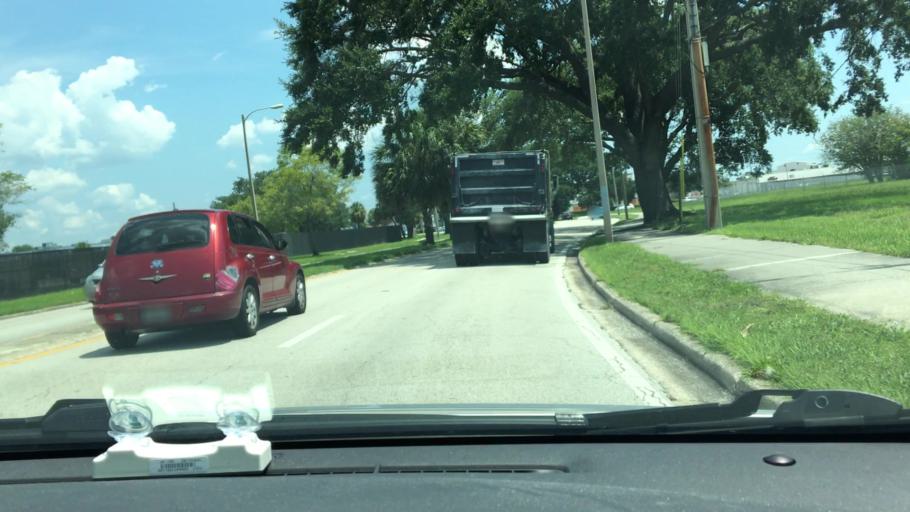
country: US
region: Florida
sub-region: Orange County
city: Orlando
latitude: 28.5499
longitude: -81.3454
